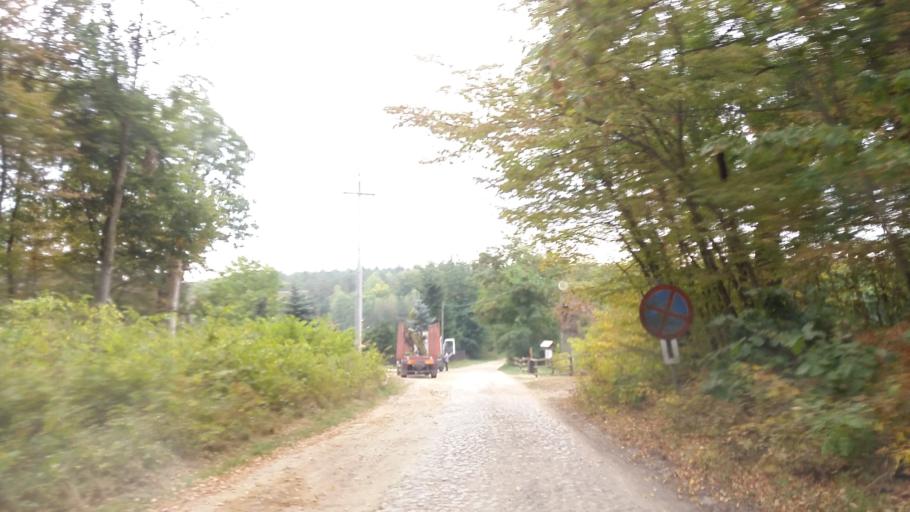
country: PL
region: West Pomeranian Voivodeship
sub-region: Powiat mysliborski
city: Barlinek
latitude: 52.9435
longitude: 15.2520
